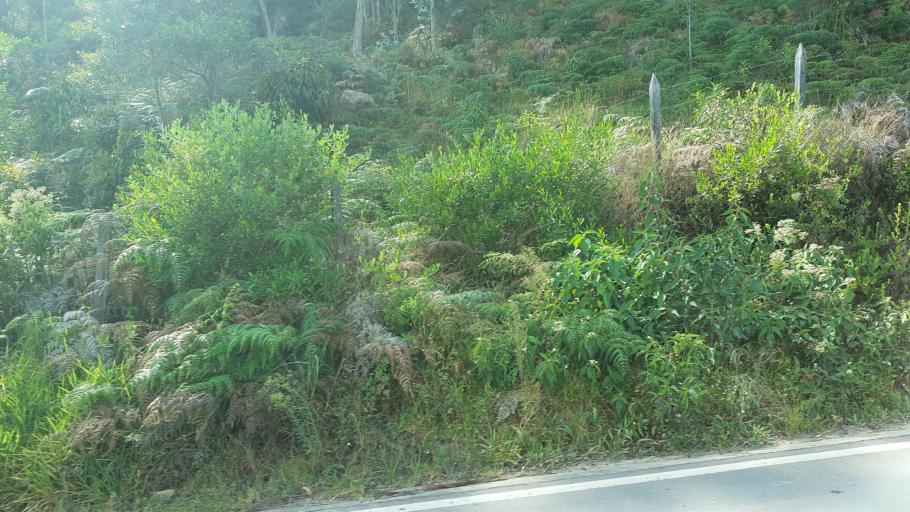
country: CO
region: Boyaca
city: Santa Sofia
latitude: 5.7704
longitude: -73.6022
